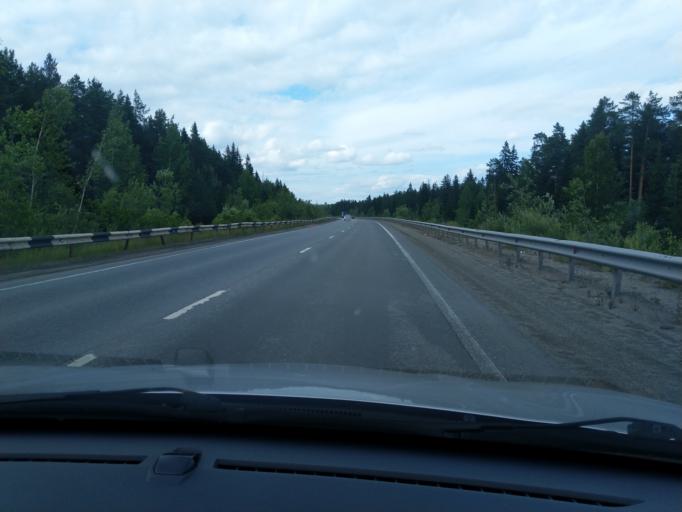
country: RU
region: Sverdlovsk
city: Nizhniy Tagil
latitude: 57.9290
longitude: 59.8617
